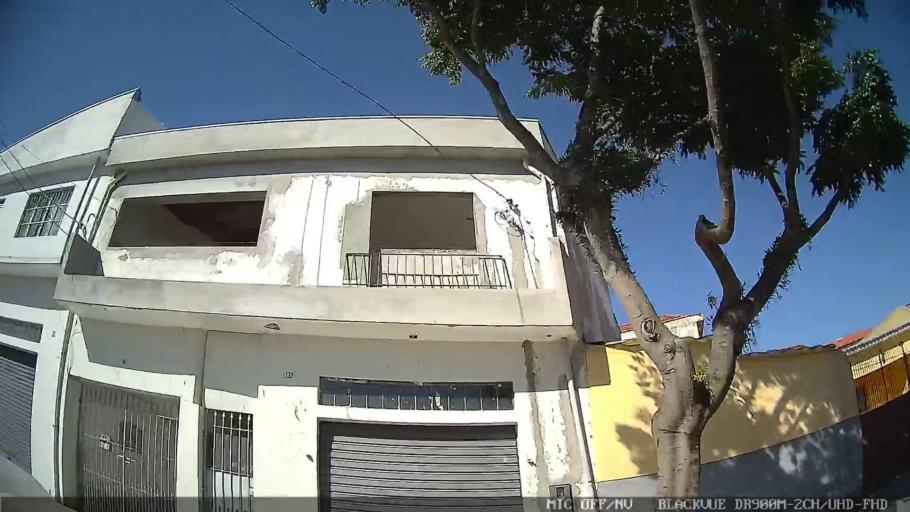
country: BR
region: Sao Paulo
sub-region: Guarulhos
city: Guarulhos
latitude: -23.5324
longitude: -46.5127
